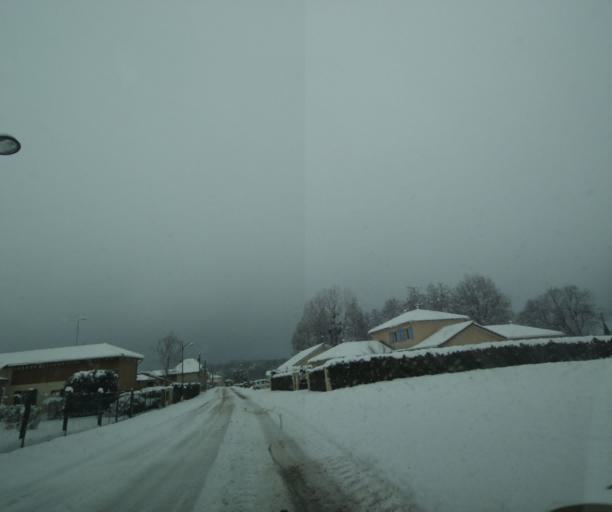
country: FR
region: Champagne-Ardenne
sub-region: Departement de la Haute-Marne
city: Montier-en-Der
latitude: 48.5355
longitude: 4.8144
